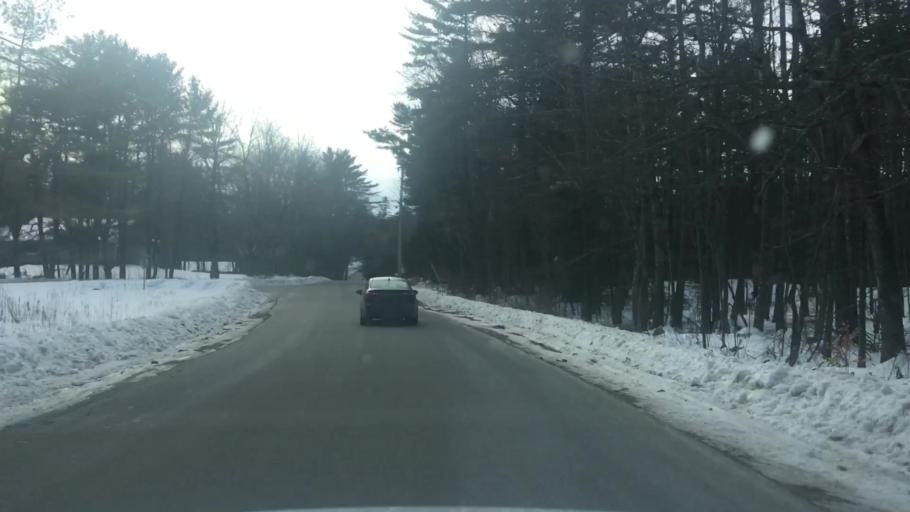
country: US
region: Maine
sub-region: Hancock County
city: Orland
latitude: 44.6247
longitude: -68.7003
